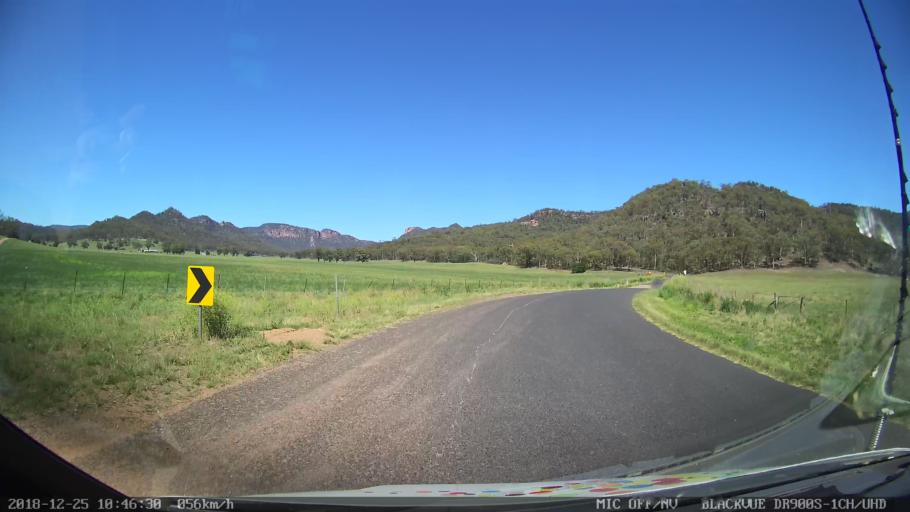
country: AU
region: New South Wales
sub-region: Upper Hunter Shire
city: Merriwa
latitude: -32.4438
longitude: 150.2848
